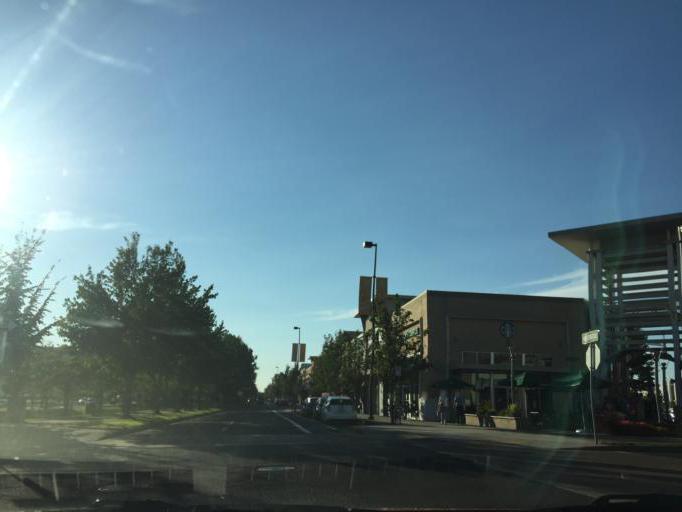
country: US
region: Oregon
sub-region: Multnomah County
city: Lents
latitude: 45.5726
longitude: -122.5574
